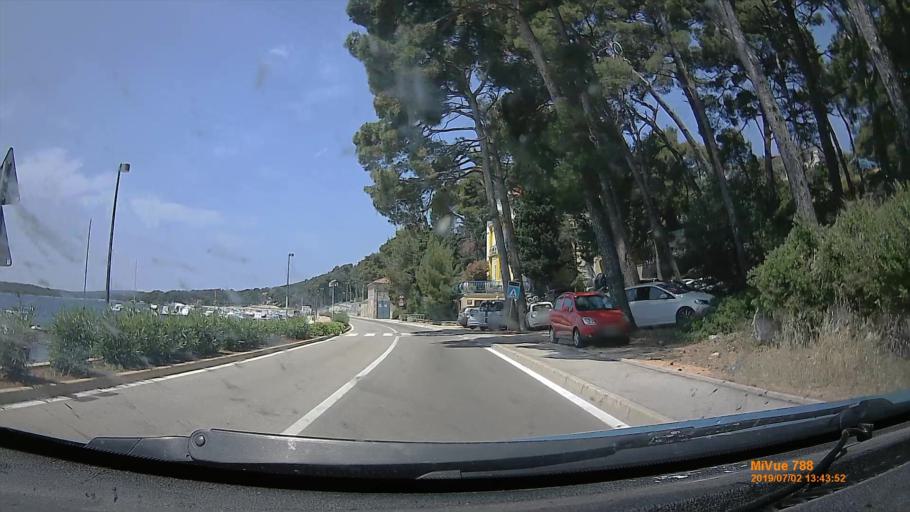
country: HR
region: Primorsko-Goranska
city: Mali Losinj
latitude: 44.5481
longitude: 14.4530
